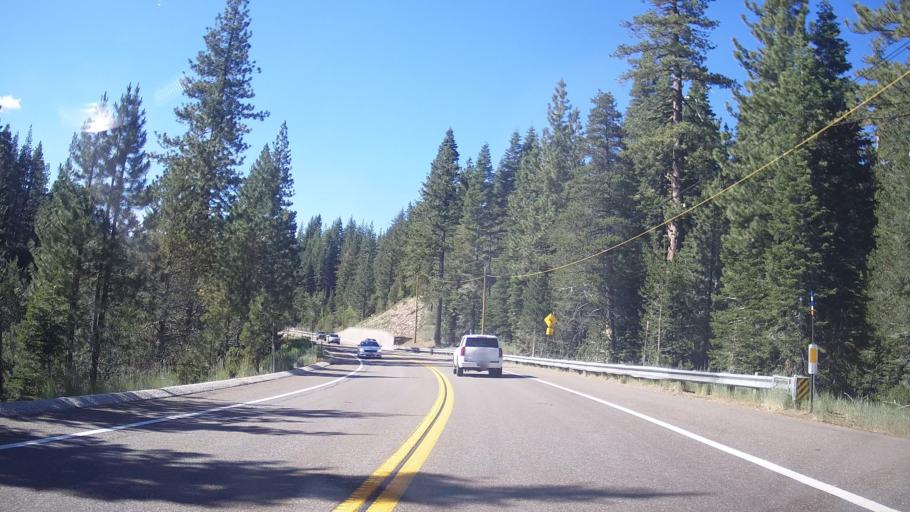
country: US
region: California
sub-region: Placer County
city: Sunnyside-Tahoe City
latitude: 39.1934
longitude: -120.1963
